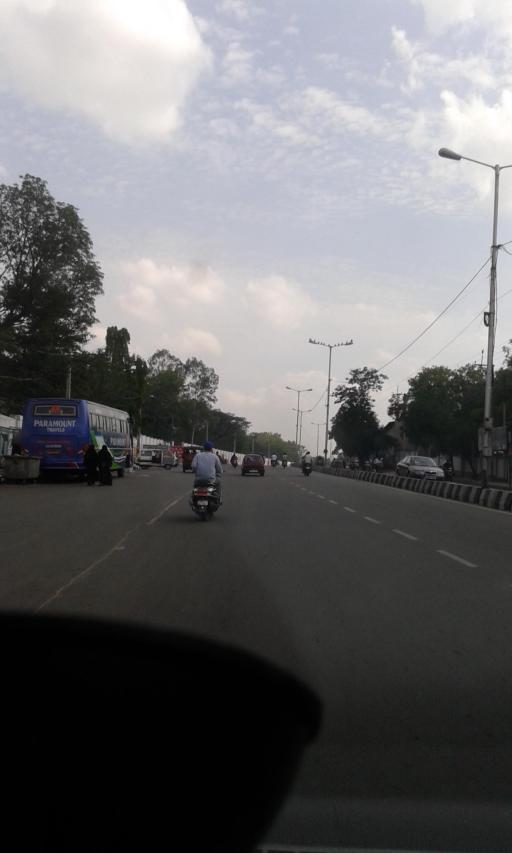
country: IN
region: Telangana
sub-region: Rangareddi
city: Gaddi Annaram
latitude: 17.3681
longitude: 78.5018
